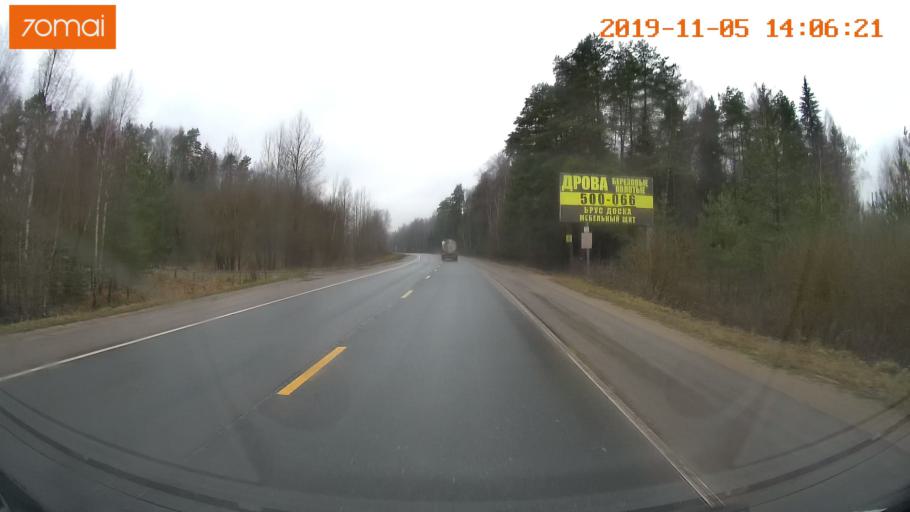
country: RU
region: Ivanovo
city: Kokhma
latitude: 56.9980
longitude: 41.1400
